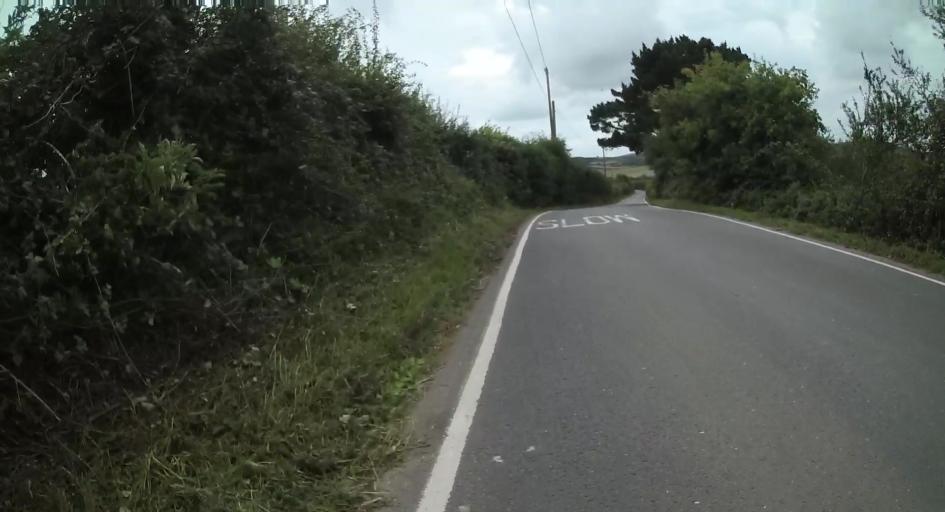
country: GB
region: England
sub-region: Isle of Wight
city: Niton
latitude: 50.6131
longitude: -1.2652
